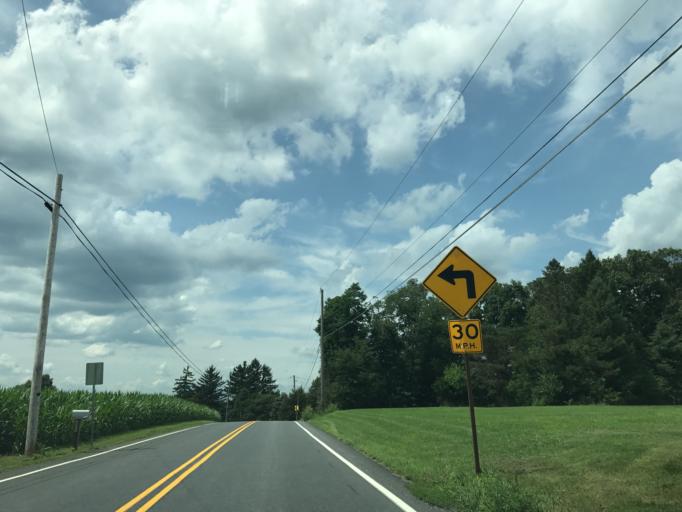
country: US
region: Pennsylvania
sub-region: Lancaster County
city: Mount Joy
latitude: 40.1804
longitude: -76.4790
